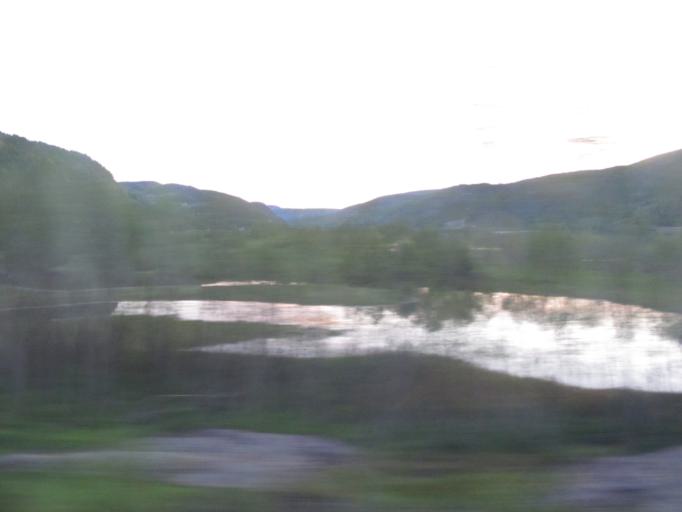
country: NO
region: Oppland
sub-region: Ringebu
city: Ringebu
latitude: 61.4535
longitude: 10.1757
